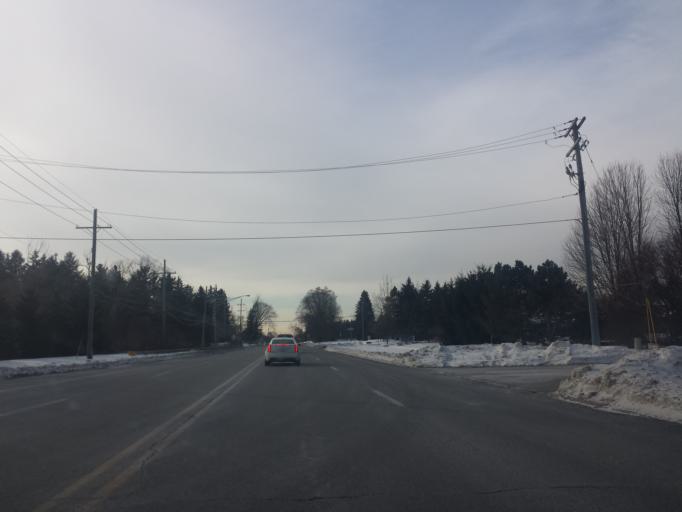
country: US
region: Michigan
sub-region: Oakland County
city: Franklin
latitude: 42.5032
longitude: -83.3393
